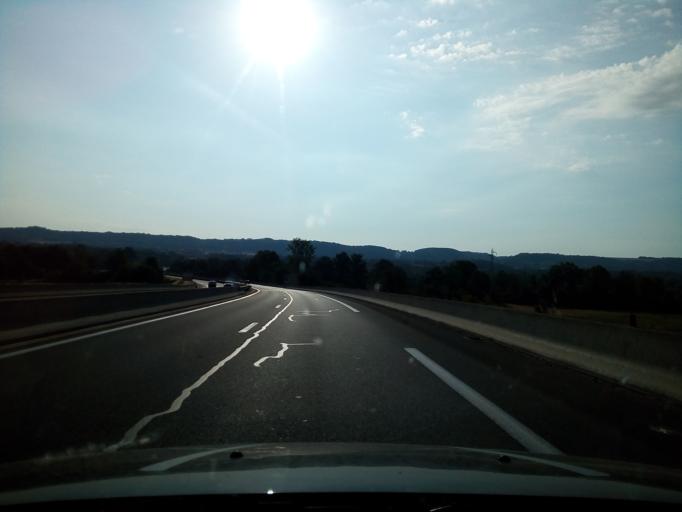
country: FR
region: Auvergne
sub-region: Departement de l'Allier
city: Saint-Victor
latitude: 46.3760
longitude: 2.5938
